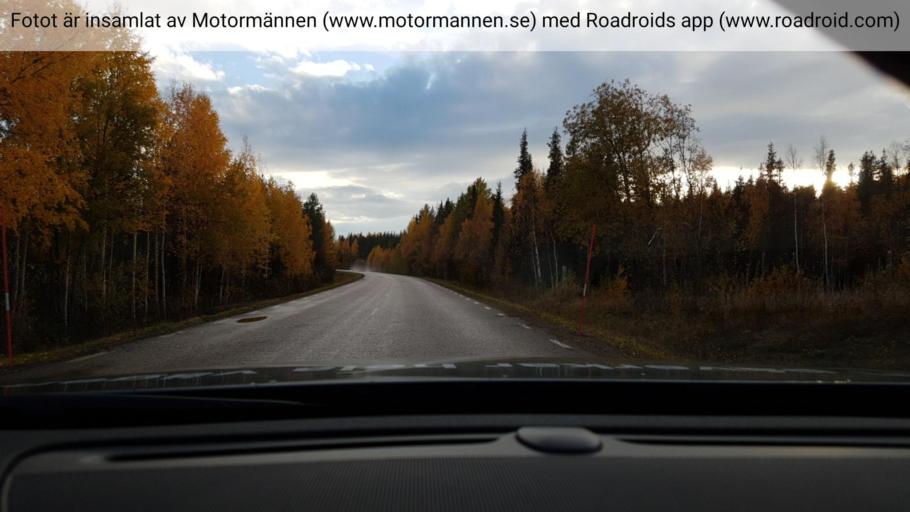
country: SE
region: Norrbotten
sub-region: Overkalix Kommun
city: OEverkalix
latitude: 66.7807
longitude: 22.7022
